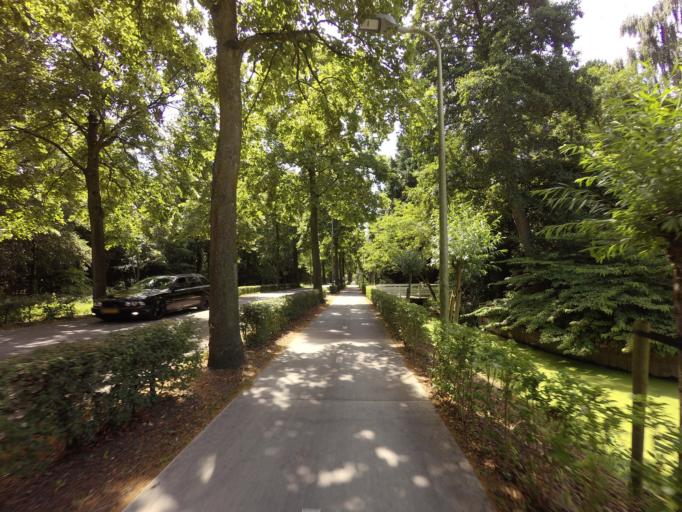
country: NL
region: South Holland
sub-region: Gemeente Teylingen
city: Sassenheim
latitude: 52.2057
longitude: 4.5095
